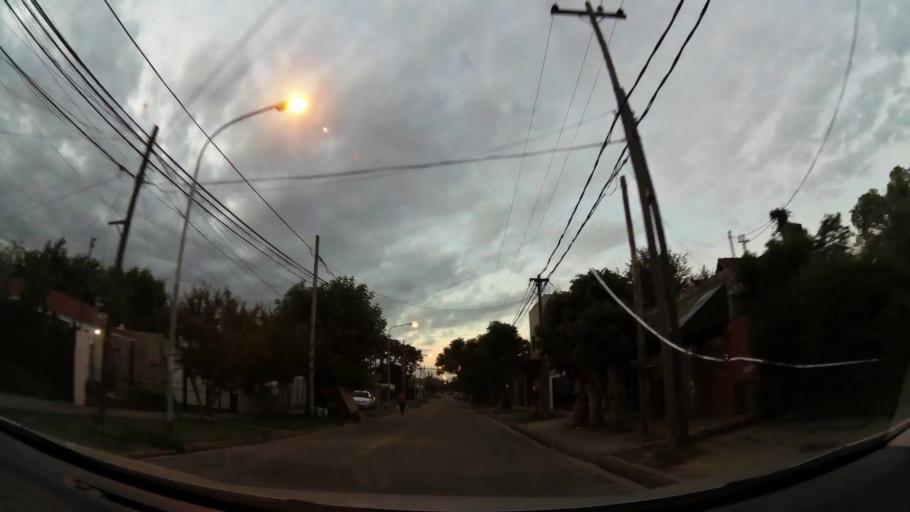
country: AR
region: Buenos Aires
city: Santa Catalina - Dique Lujan
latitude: -34.4144
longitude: -58.6855
